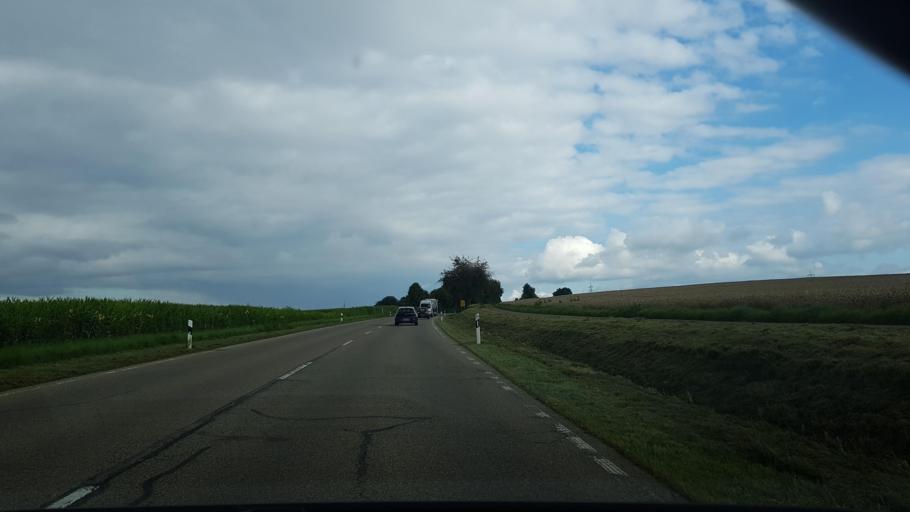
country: DE
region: Baden-Wuerttemberg
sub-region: Tuebingen Region
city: Laichingen
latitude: 48.4610
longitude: 9.6930
